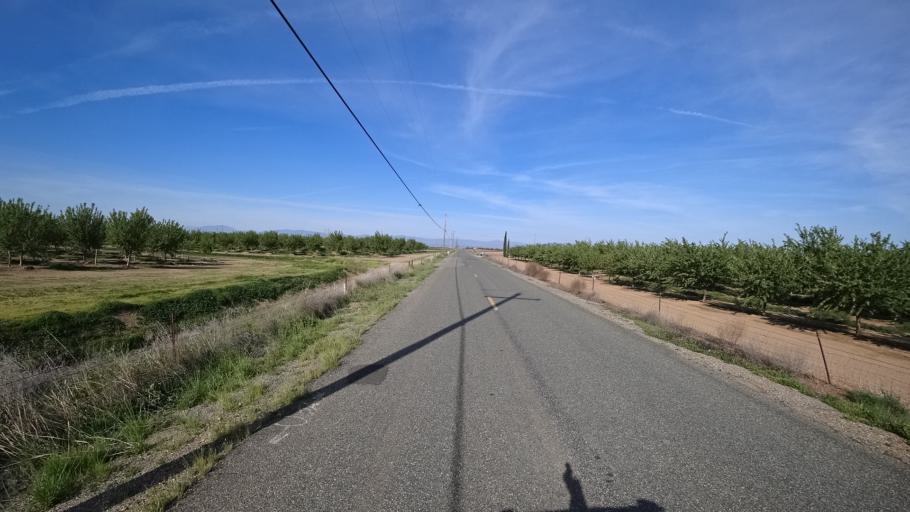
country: US
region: California
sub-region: Glenn County
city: Orland
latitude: 39.6683
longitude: -122.2567
